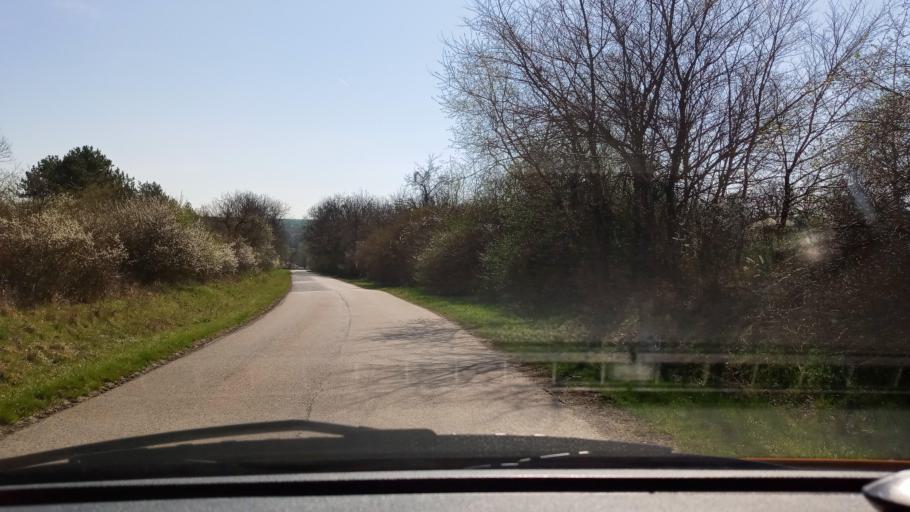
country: HU
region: Baranya
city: Kozarmisleny
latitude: 46.0734
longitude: 18.3584
